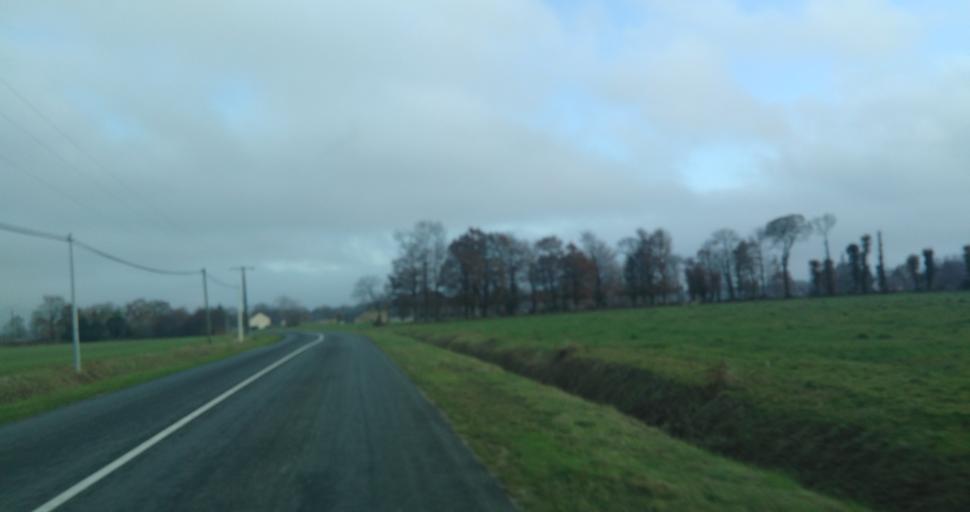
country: FR
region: Brittany
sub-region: Departement d'Ille-et-Vilaine
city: Boisgervilly
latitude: 48.1650
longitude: -2.0890
